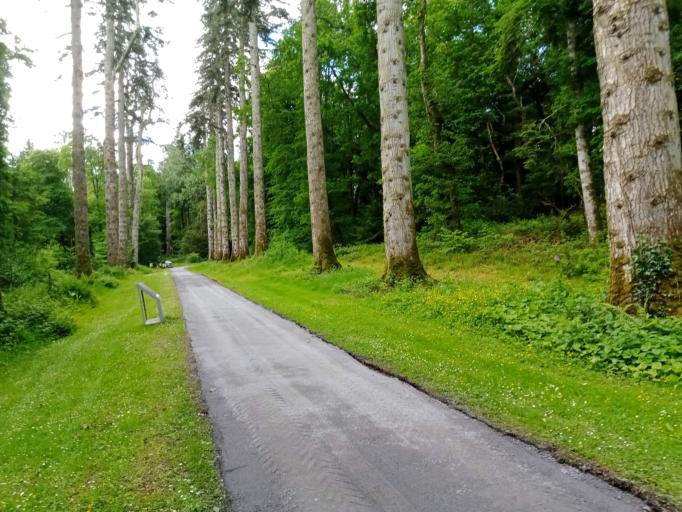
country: IE
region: Leinster
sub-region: Kilkenny
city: Thomastown
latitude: 52.4721
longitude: -7.0575
